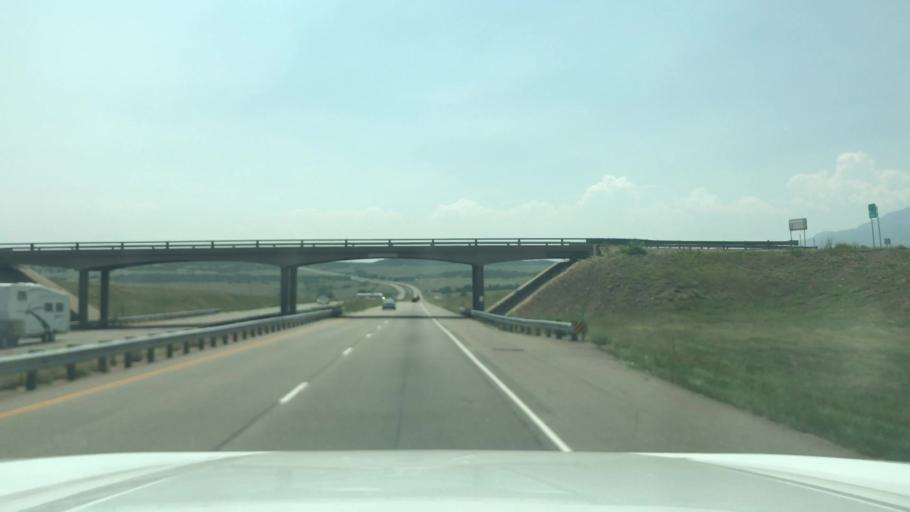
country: US
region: Colorado
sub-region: Pueblo County
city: Colorado City
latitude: 37.9259
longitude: -104.8219
